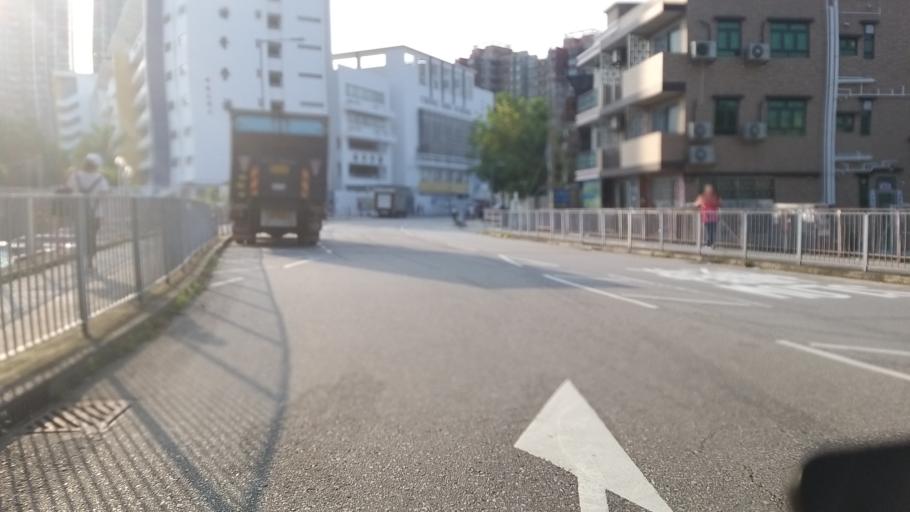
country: HK
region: Yuen Long
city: Yuen Long Kau Hui
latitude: 22.4480
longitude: 114.0341
